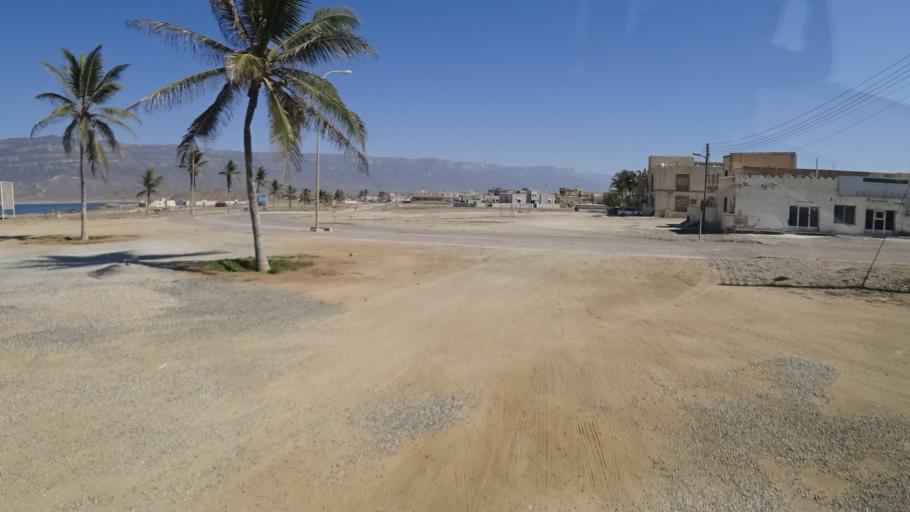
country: OM
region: Zufar
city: Salalah
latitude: 16.9791
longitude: 54.6868
